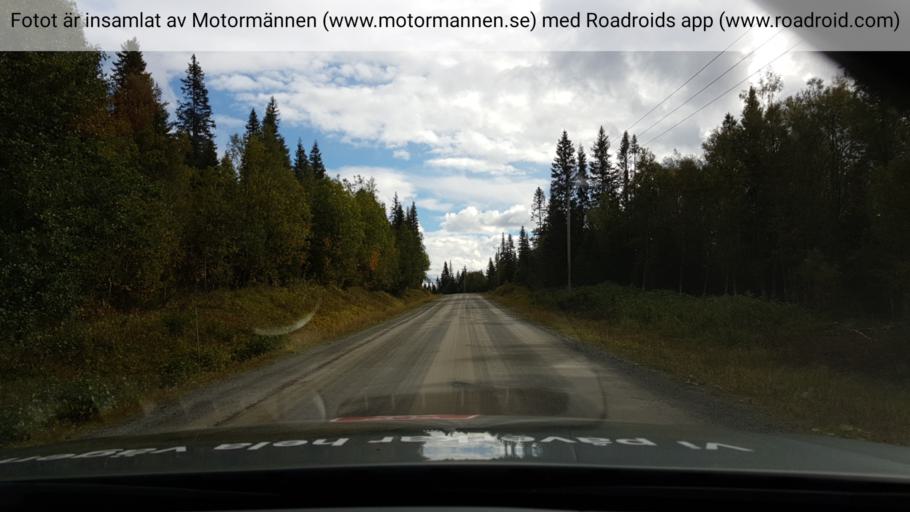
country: SE
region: Jaemtland
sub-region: Are Kommun
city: Are
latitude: 63.7001
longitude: 12.7736
